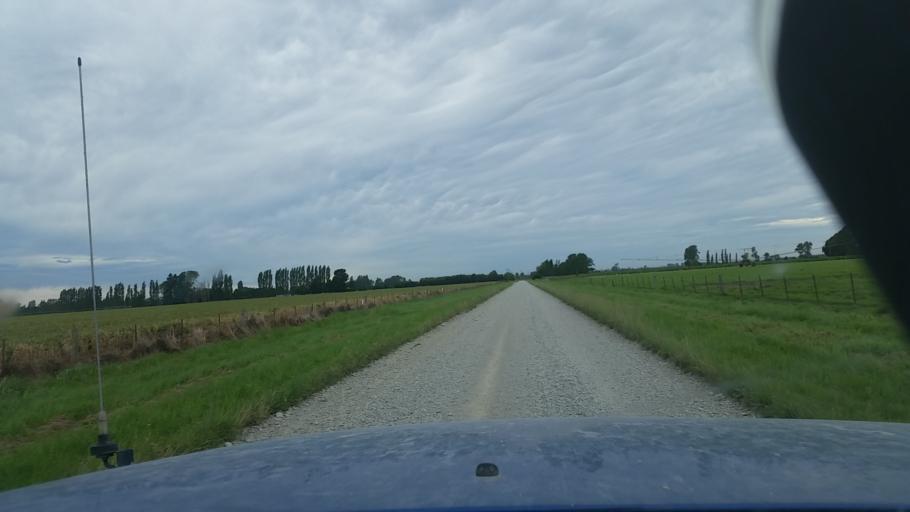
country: NZ
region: Canterbury
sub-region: Ashburton District
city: Ashburton
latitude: -43.8203
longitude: 171.6353
